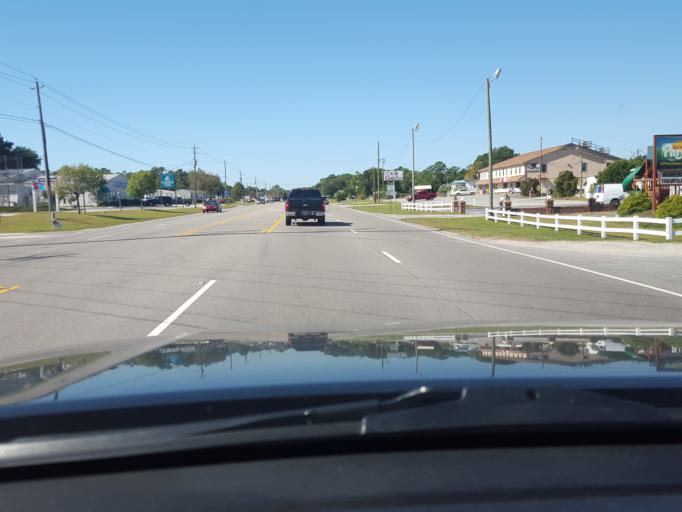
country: US
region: North Carolina
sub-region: New Hanover County
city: Seagate
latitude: 34.2088
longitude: -77.8524
